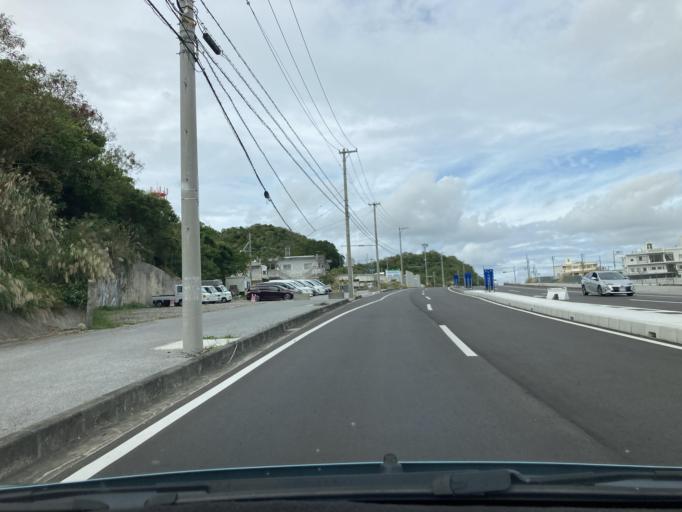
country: JP
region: Okinawa
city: Tomigusuku
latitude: 26.1667
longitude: 127.6778
